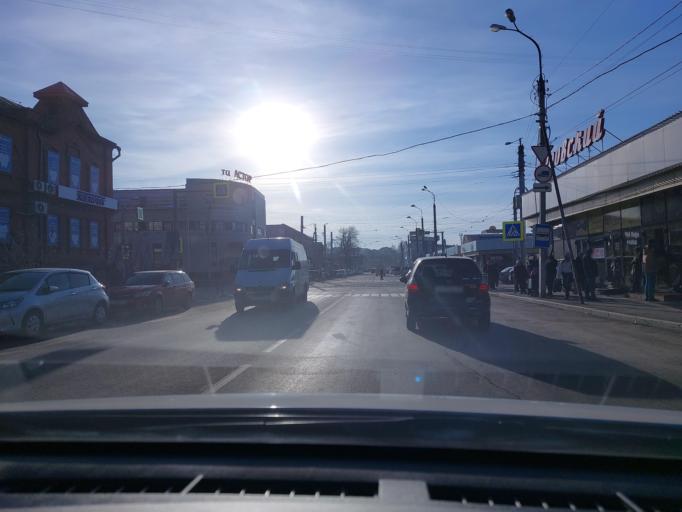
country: RU
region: Irkutsk
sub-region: Irkutskiy Rayon
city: Irkutsk
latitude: 52.2813
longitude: 104.3002
